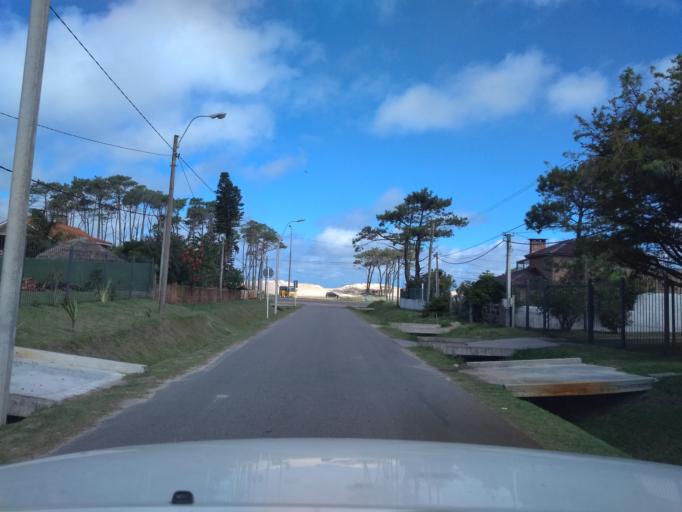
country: UY
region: Canelones
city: Barra de Carrasco
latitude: -34.8407
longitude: -55.9661
